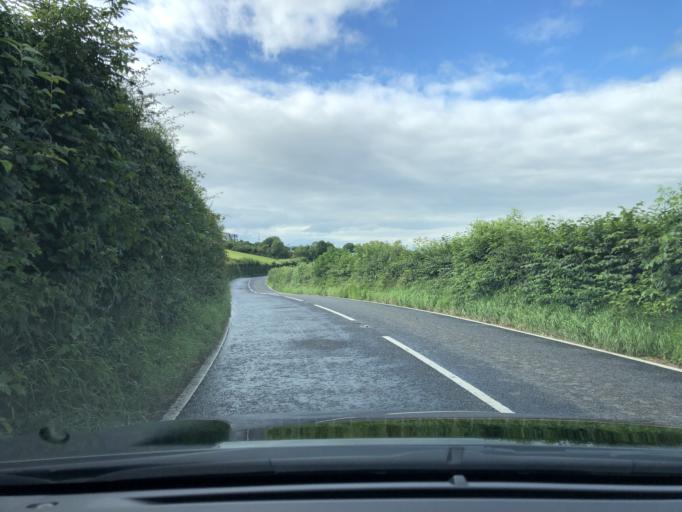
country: GB
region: Northern Ireland
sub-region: Down District
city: Dundrum
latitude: 54.2579
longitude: -5.7798
